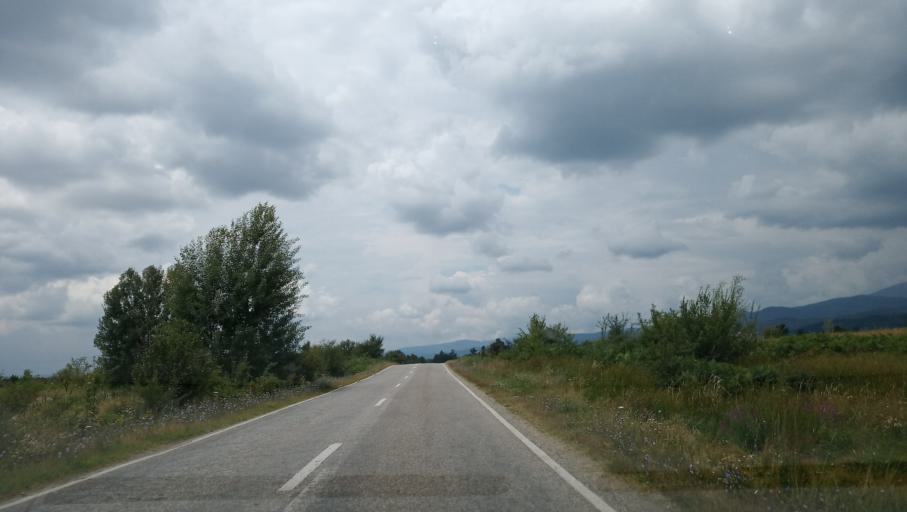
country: RO
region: Gorj
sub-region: Comuna Runcu
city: Valea Mare
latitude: 45.0867
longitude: 23.0881
